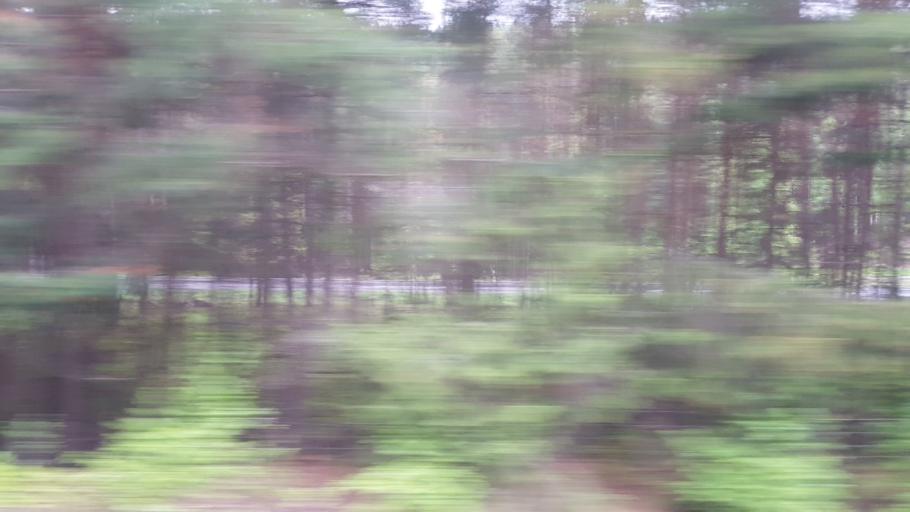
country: NO
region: Oppland
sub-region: Ringebu
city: Ringebu
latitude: 61.5505
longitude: 10.0760
